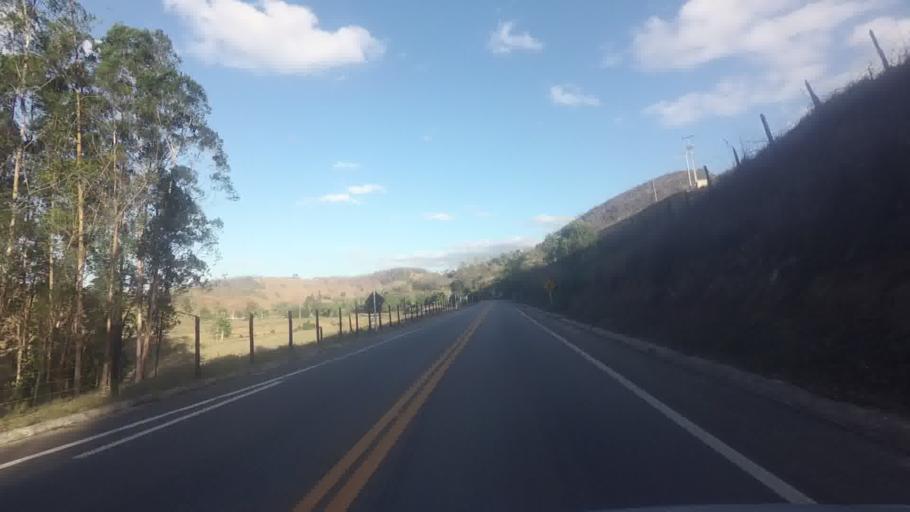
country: BR
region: Espirito Santo
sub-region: Cachoeiro De Itapemirim
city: Cachoeiro de Itapemirim
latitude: -20.8254
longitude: -41.2160
